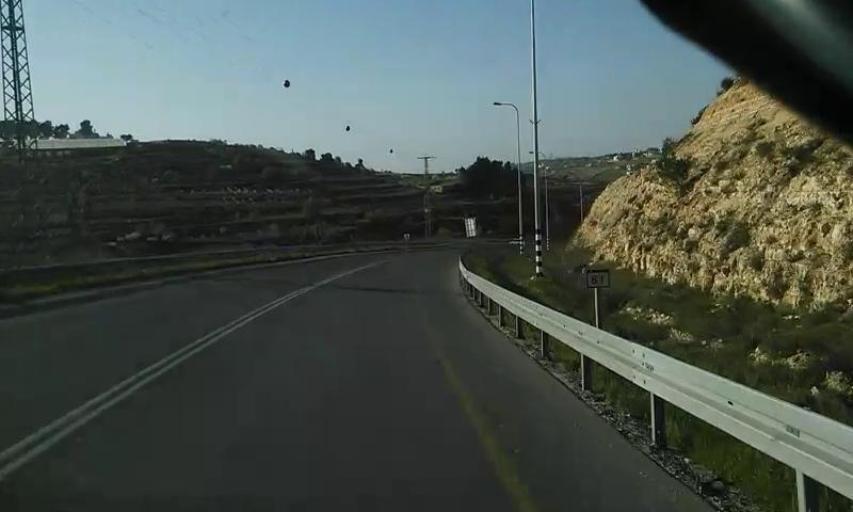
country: PS
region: West Bank
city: Halhul
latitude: 31.5881
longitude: 35.1167
